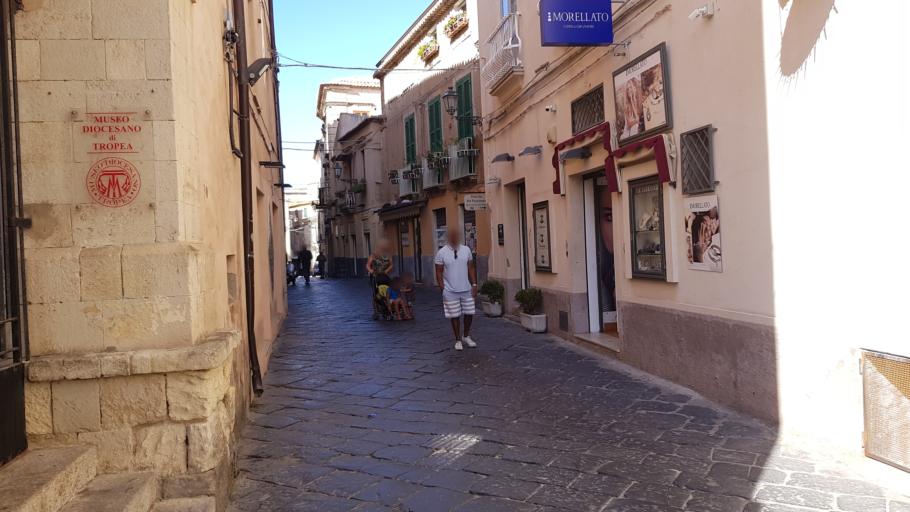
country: IT
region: Calabria
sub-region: Provincia di Vibo-Valentia
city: Tropea
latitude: 38.6782
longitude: 15.8985
